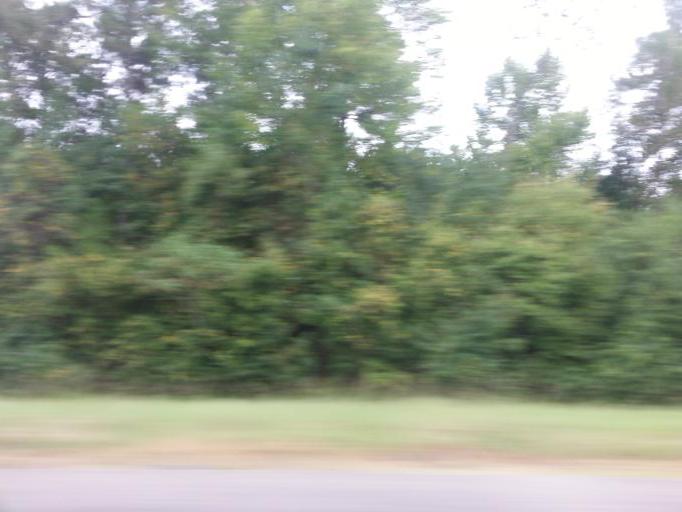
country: US
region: Alabama
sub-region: Butler County
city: Georgiana
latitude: 31.6150
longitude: -86.8114
